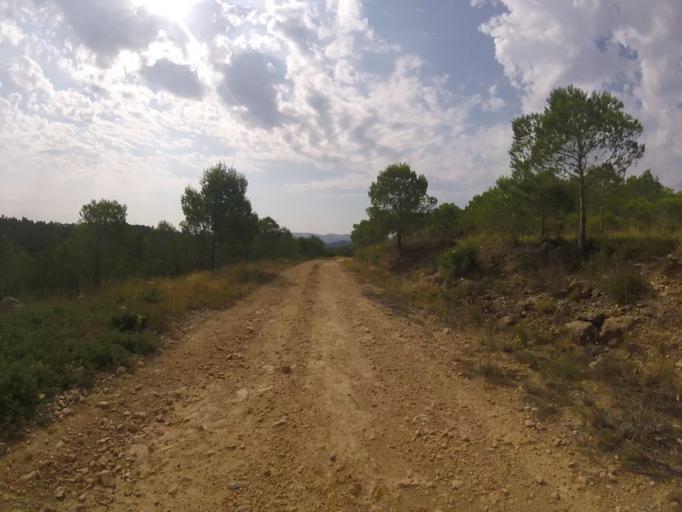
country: ES
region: Valencia
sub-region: Provincia de Castello
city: Alcala de Xivert
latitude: 40.3785
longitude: 0.2094
